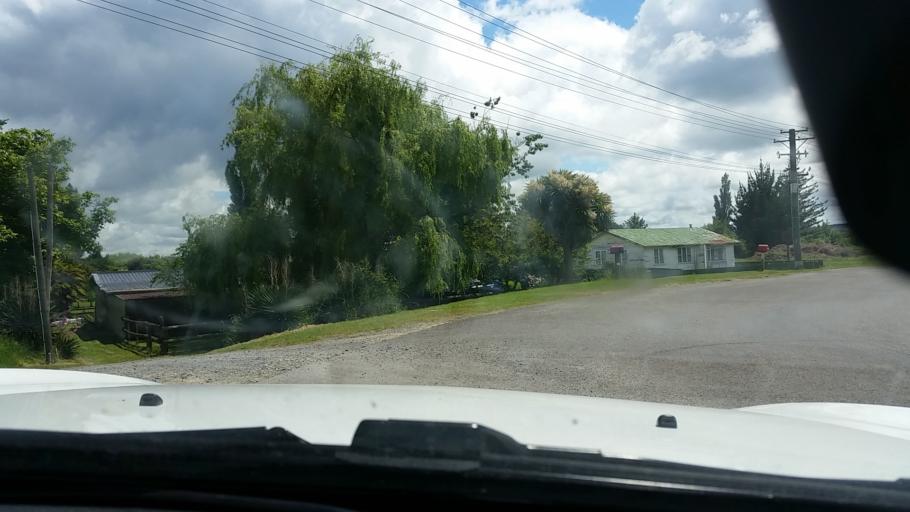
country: NZ
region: Bay of Plenty
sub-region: Rotorua District
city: Rotorua
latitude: -38.0797
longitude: 176.3245
